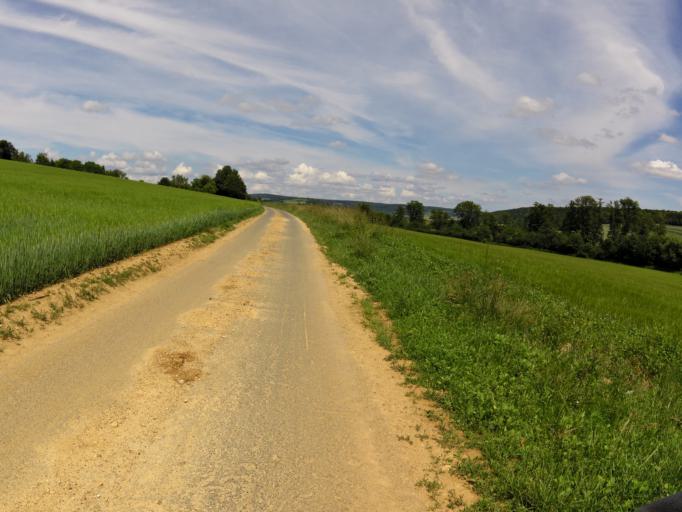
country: FR
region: Champagne-Ardenne
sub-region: Departement des Ardennes
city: Mouzon
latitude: 49.5272
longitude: 5.0910
